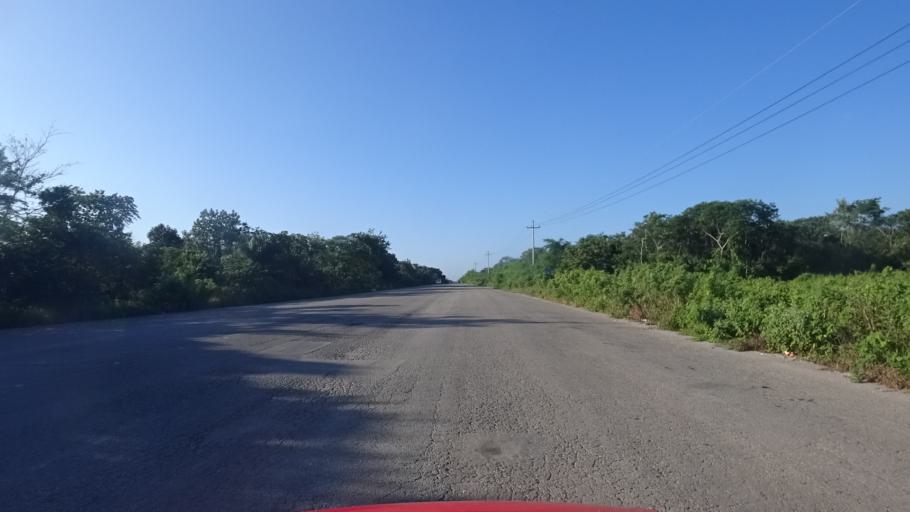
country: MX
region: Yucatan
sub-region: Tizimin
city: Tizimin
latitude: 21.1502
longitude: -88.1832
